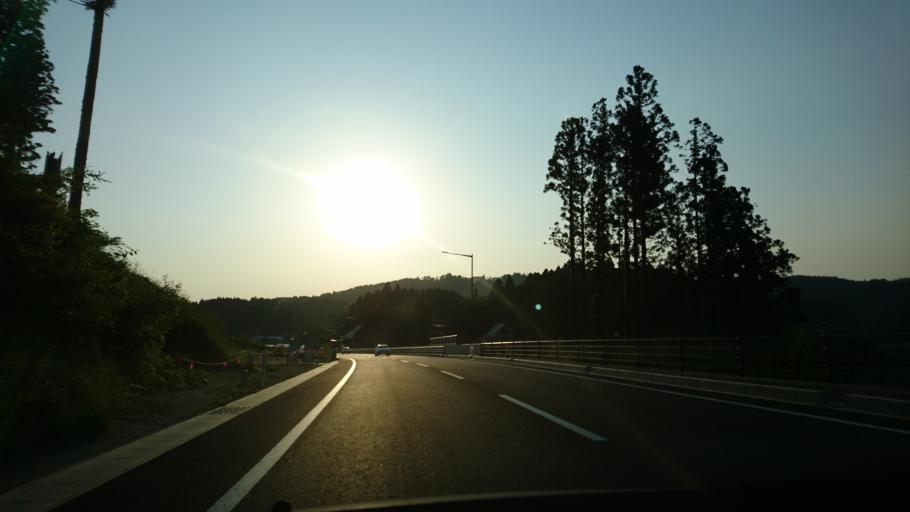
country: JP
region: Iwate
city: Ichinoseki
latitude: 38.9366
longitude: 141.4351
